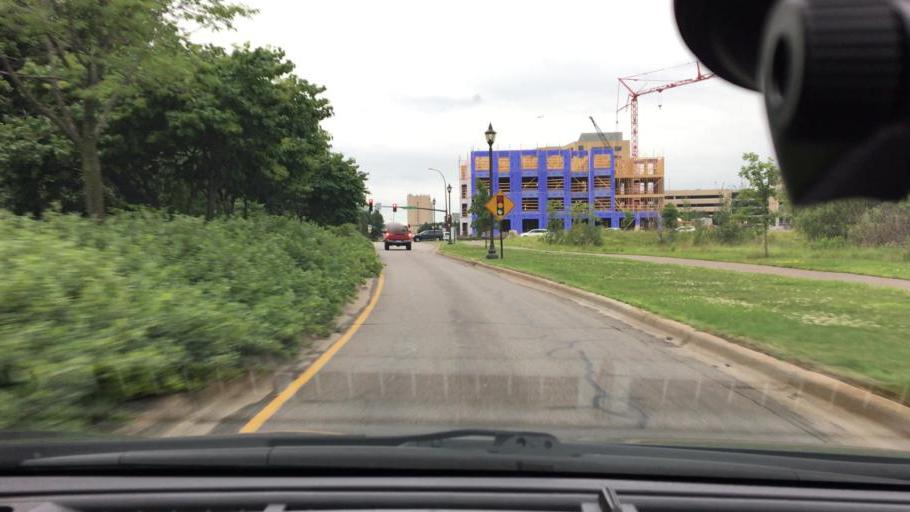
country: US
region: Minnesota
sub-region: Hennepin County
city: Saint Louis Park
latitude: 44.9758
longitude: -93.3525
